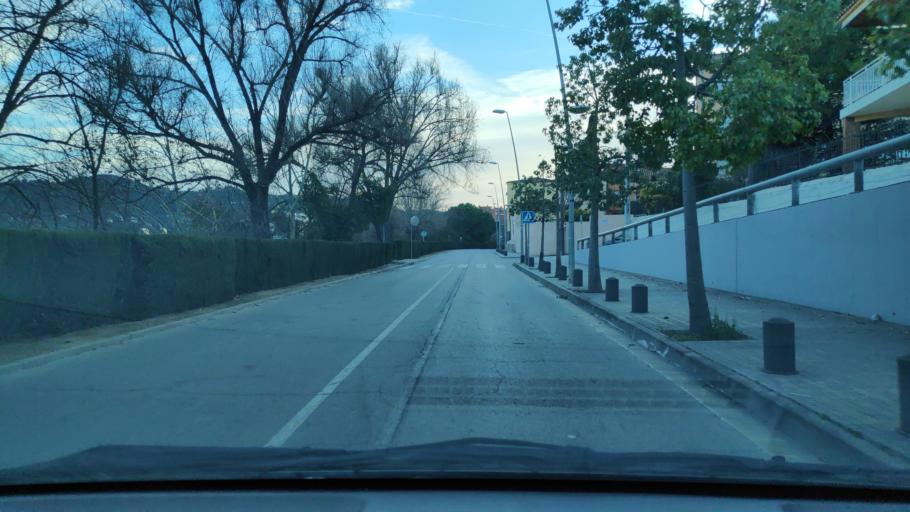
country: ES
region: Catalonia
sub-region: Provincia de Barcelona
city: Montmelo
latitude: 41.5558
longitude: 2.2515
